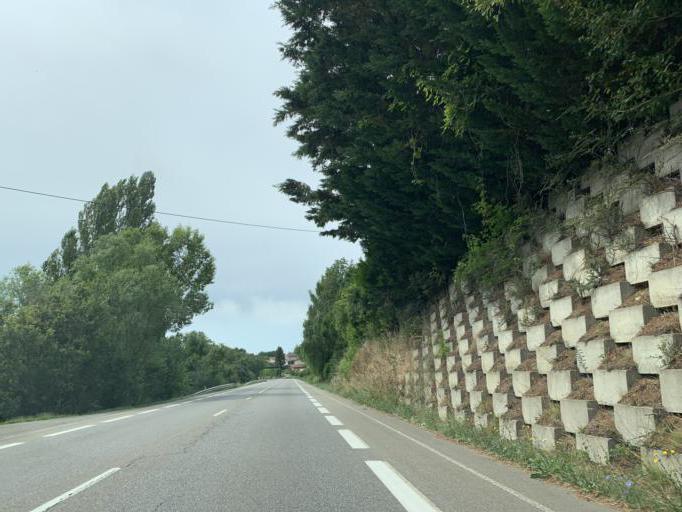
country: FR
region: Provence-Alpes-Cote d'Azur
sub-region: Departement des Hautes-Alpes
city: Gap
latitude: 44.5466
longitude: 6.0239
